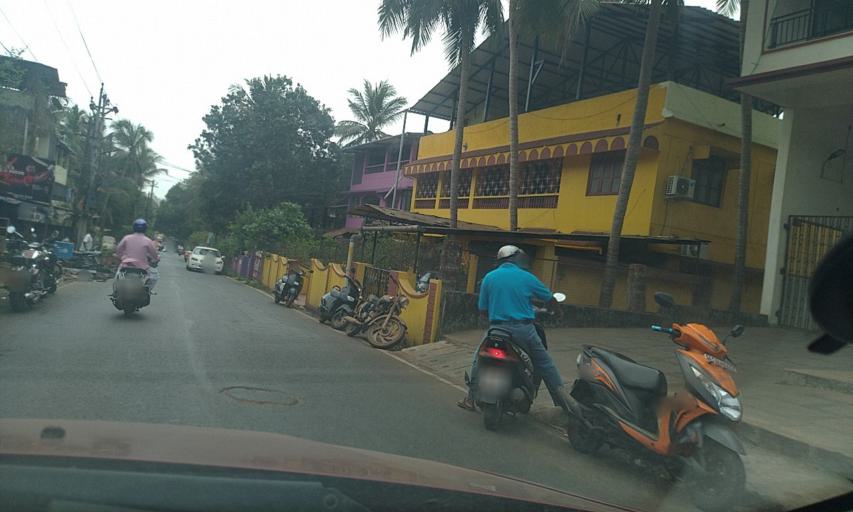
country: IN
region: Goa
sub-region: North Goa
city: Mapuca
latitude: 15.5942
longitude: 73.8009
